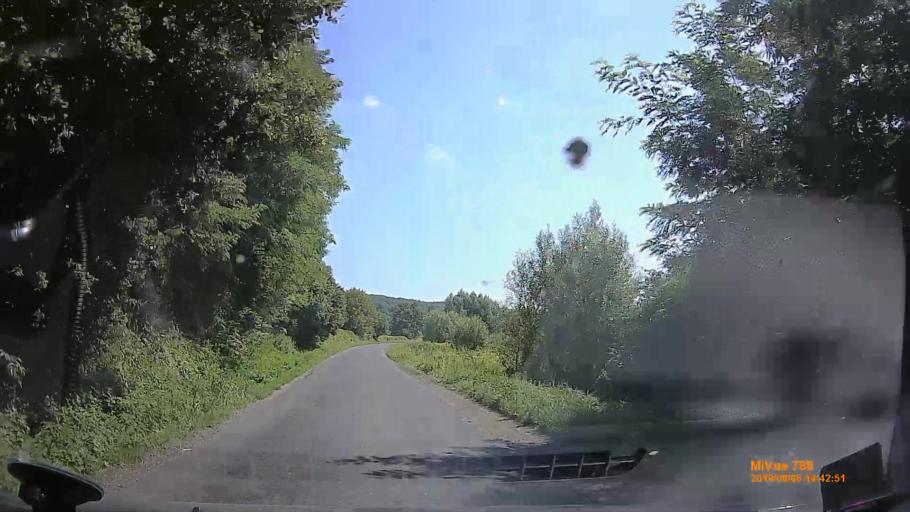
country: HU
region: Zala
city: Nagykanizsa
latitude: 46.5373
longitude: 17.0503
